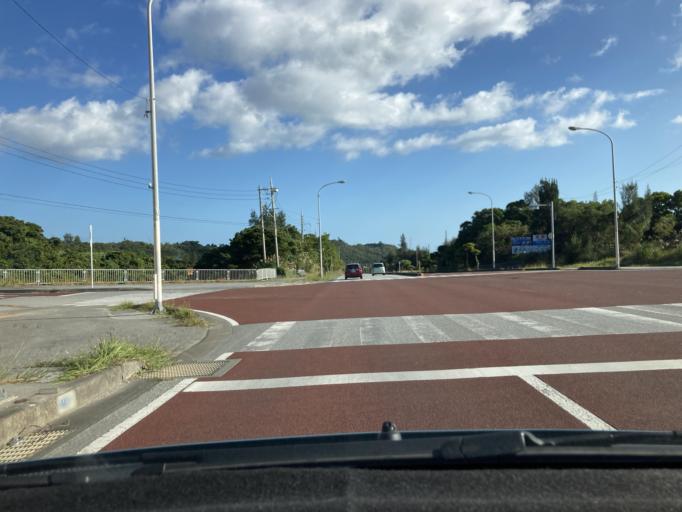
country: JP
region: Okinawa
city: Ishikawa
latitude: 26.4037
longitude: 127.8243
